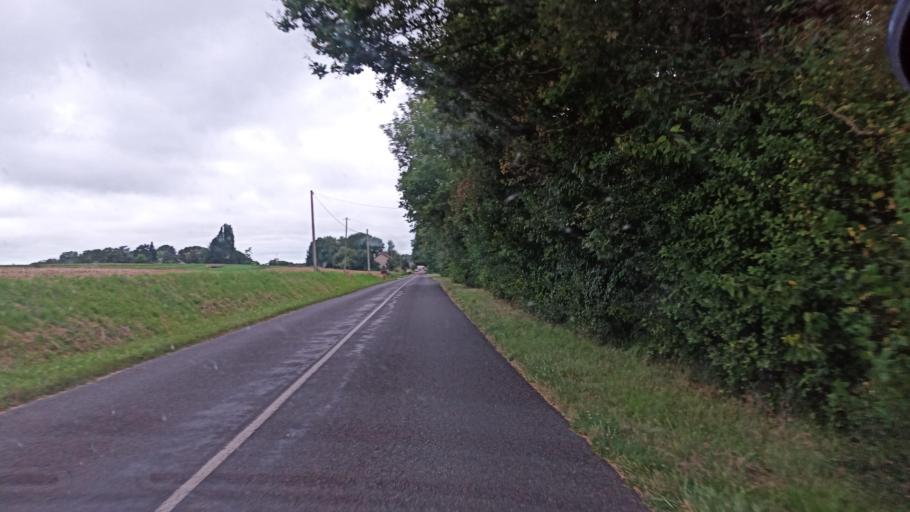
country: FR
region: Ile-de-France
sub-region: Departement de Seine-et-Marne
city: Voulx
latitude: 48.2773
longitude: 2.9814
